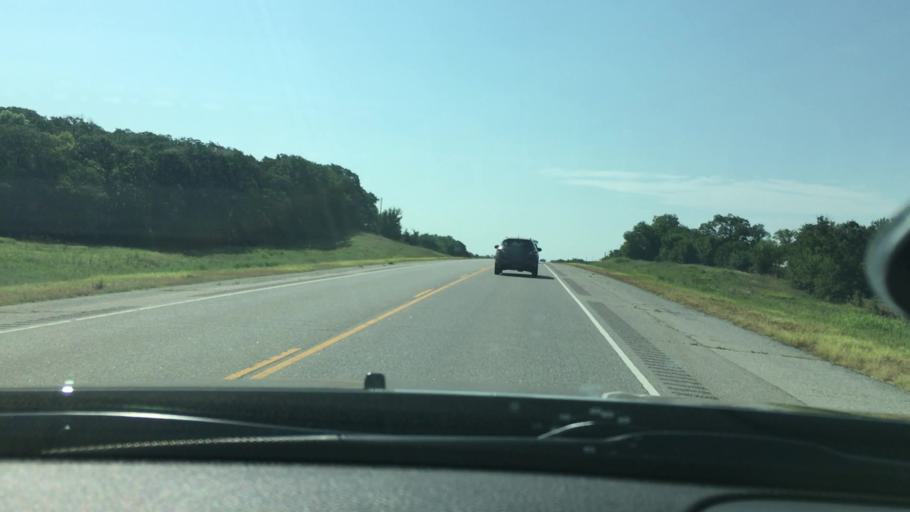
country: US
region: Oklahoma
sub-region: Pontotoc County
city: Ada
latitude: 34.6290
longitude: -96.4670
